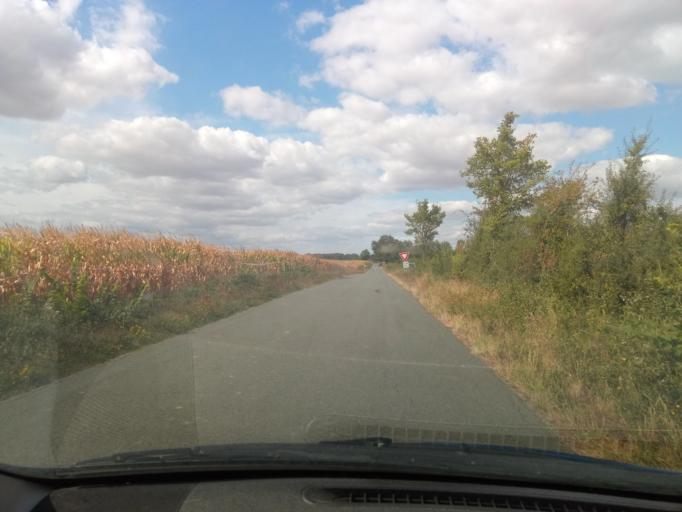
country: FR
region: Poitou-Charentes
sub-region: Departement de la Vienne
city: Montmorillon
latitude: 46.4966
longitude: 0.8103
